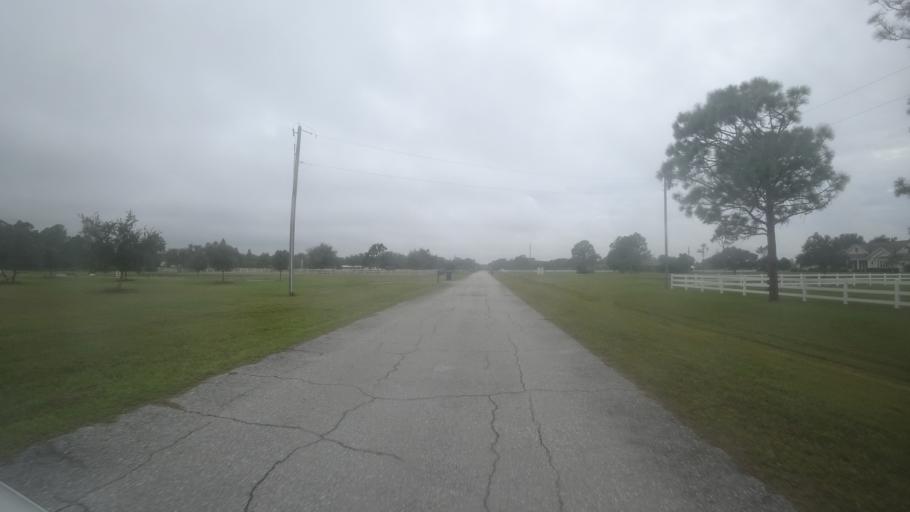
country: US
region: Florida
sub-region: Sarasota County
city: The Meadows
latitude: 27.3983
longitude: -82.3302
